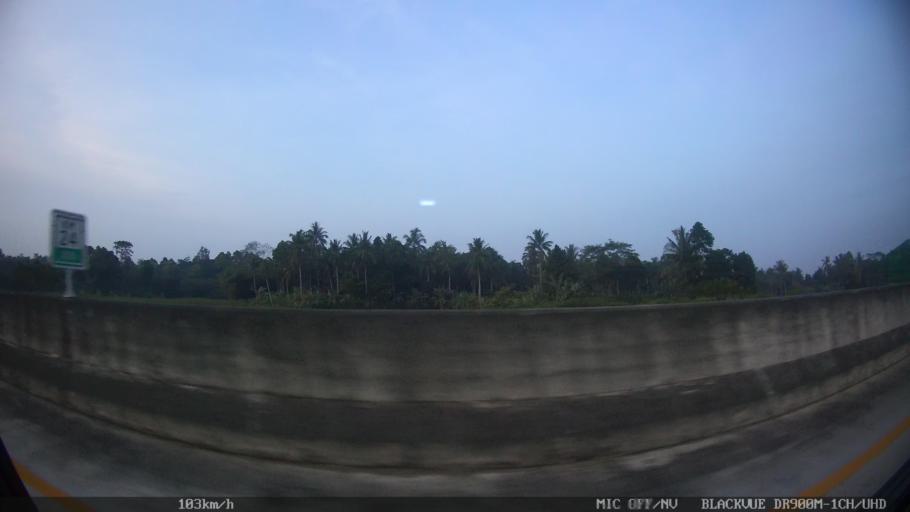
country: ID
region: Lampung
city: Pasuruan
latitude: -5.7075
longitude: 105.6427
